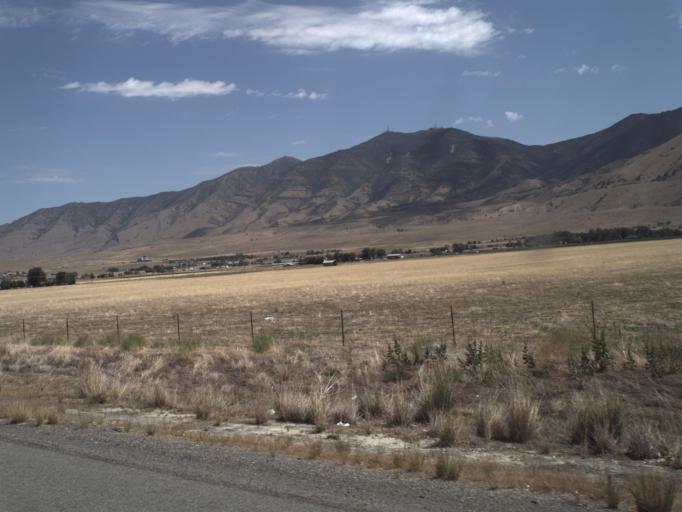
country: US
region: Utah
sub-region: Tooele County
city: Erda
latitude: 40.5920
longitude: -112.2939
